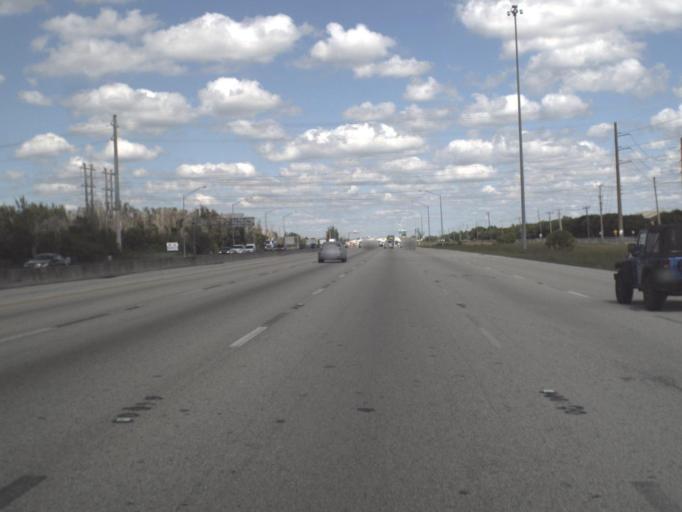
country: US
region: Florida
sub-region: Miami-Dade County
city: Doral
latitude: 25.8160
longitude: -80.3864
